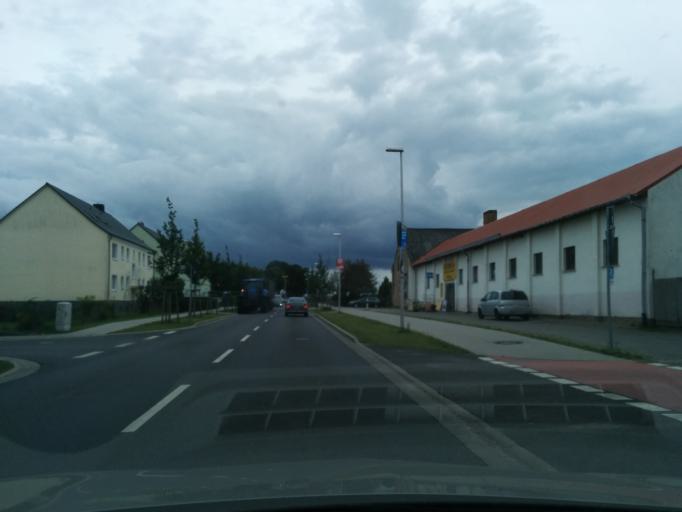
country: DE
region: Mecklenburg-Vorpommern
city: Zussow
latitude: 53.9739
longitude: 13.5441
